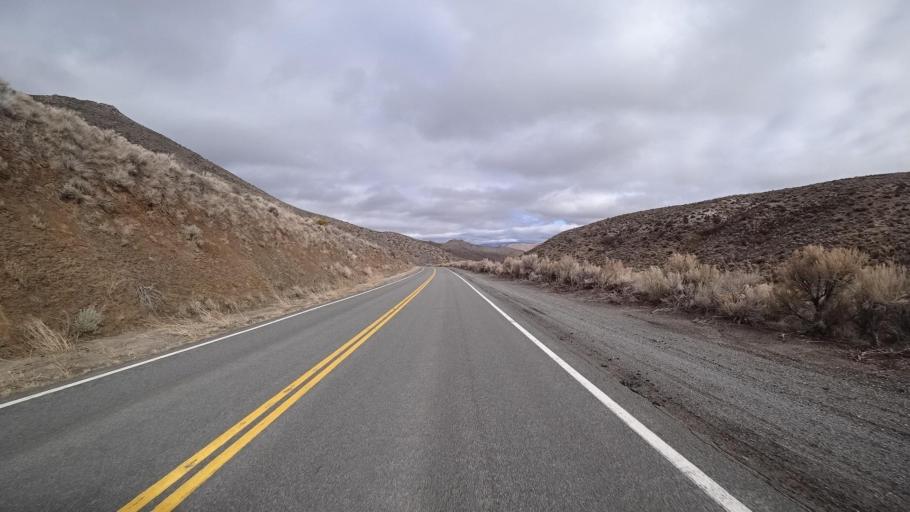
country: US
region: Nevada
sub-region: Washoe County
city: Cold Springs
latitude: 39.8151
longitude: -119.9344
